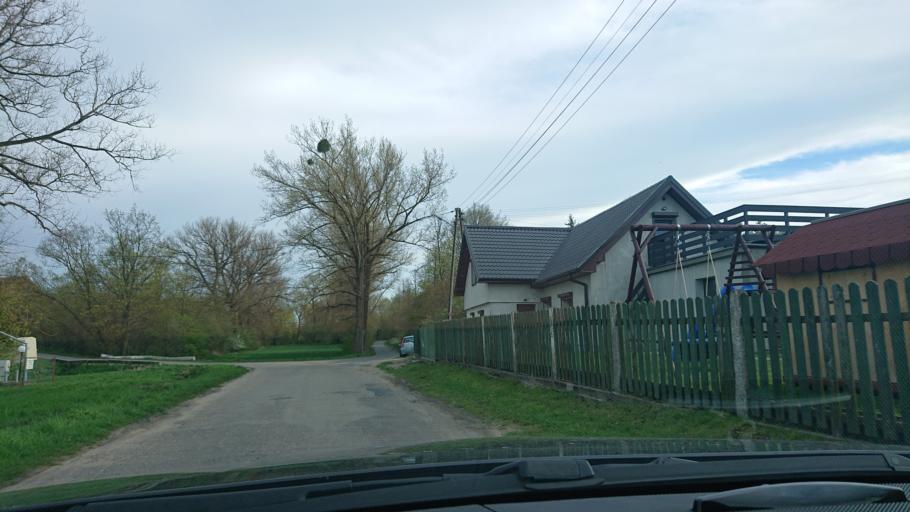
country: PL
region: Greater Poland Voivodeship
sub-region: Powiat gnieznienski
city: Lubowo
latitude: 52.5755
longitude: 17.4708
